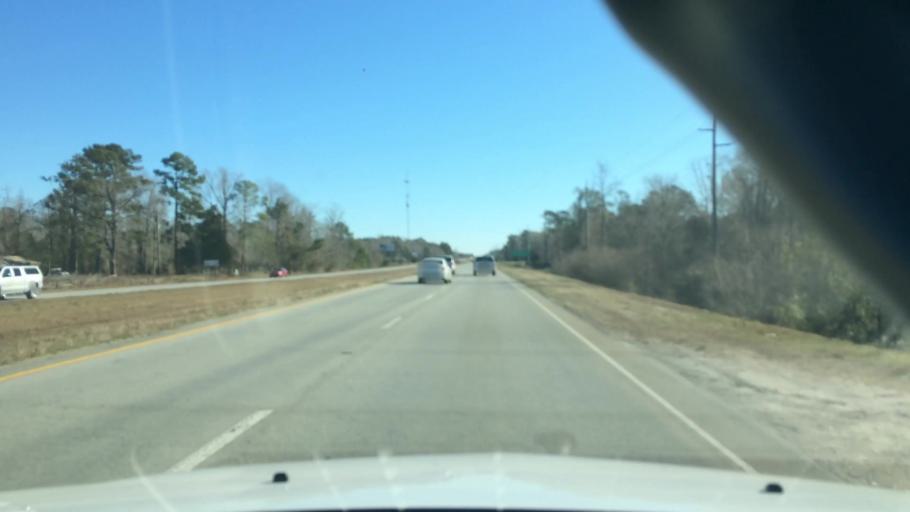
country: US
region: North Carolina
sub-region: Brunswick County
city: Sunset Beach
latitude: 33.9468
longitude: -78.4993
